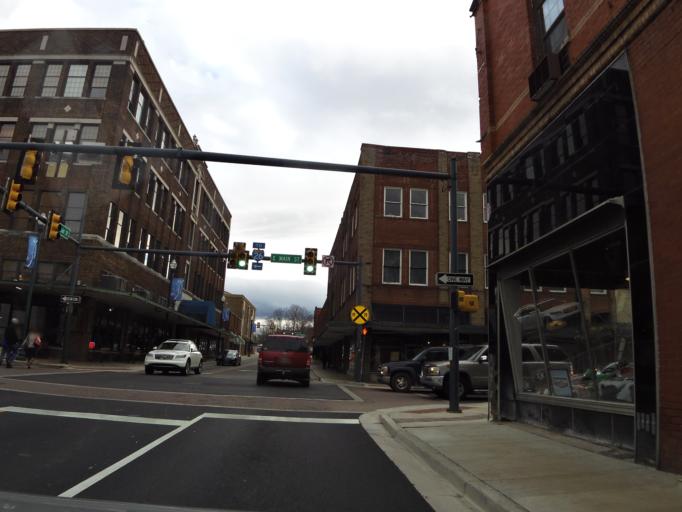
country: US
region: Tennessee
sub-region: Washington County
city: Johnson City
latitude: 36.3173
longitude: -82.3508
